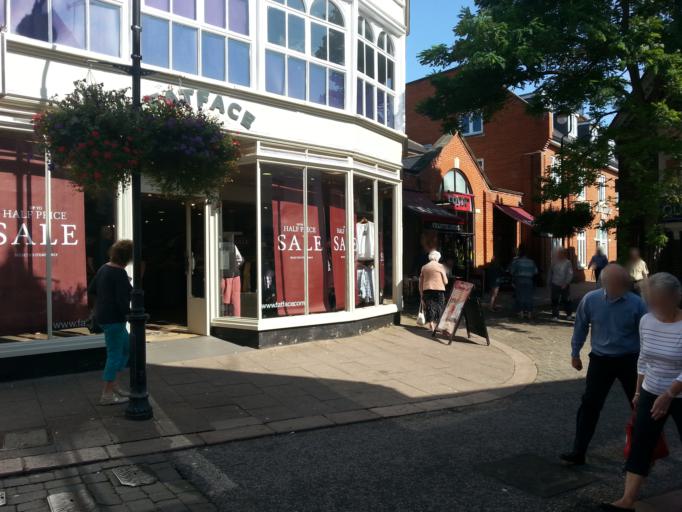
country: GB
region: England
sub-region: Suffolk
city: Woodbridge
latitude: 52.0929
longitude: 1.3174
